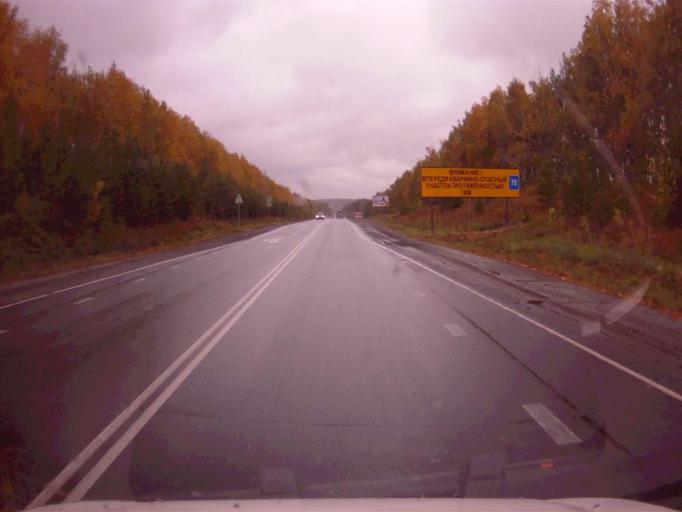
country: RU
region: Chelyabinsk
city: Roshchino
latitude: 55.3616
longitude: 61.2169
